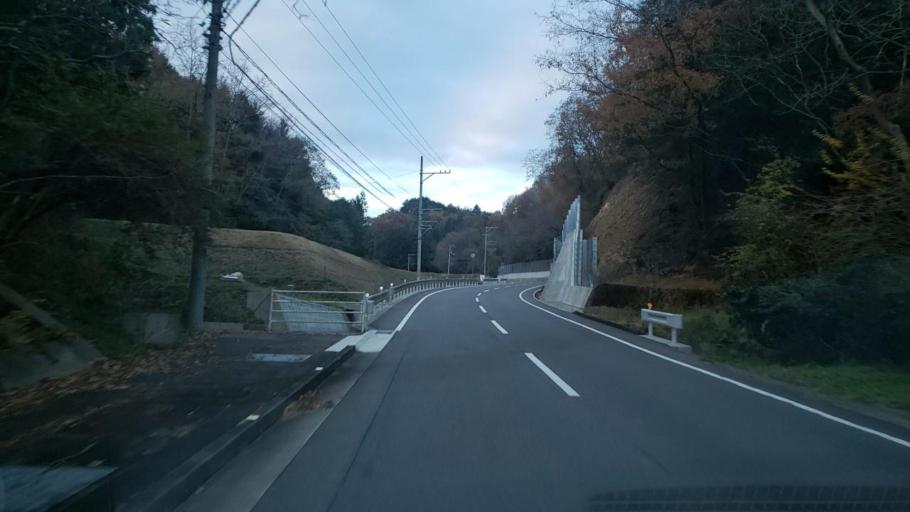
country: JP
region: Kagawa
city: Shido
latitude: 34.1953
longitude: 134.2507
